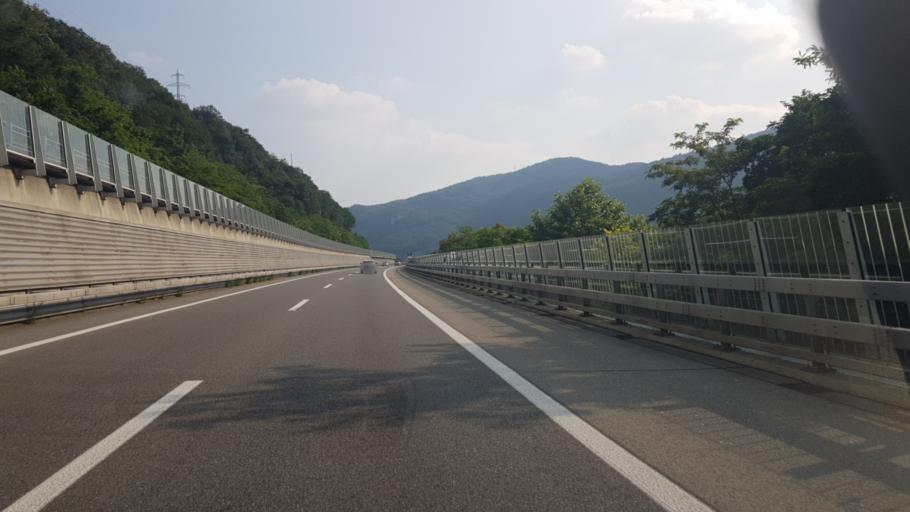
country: CH
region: Ticino
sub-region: Mendrisio District
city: Riva San Vitale
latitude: 45.9021
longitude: 8.9808
